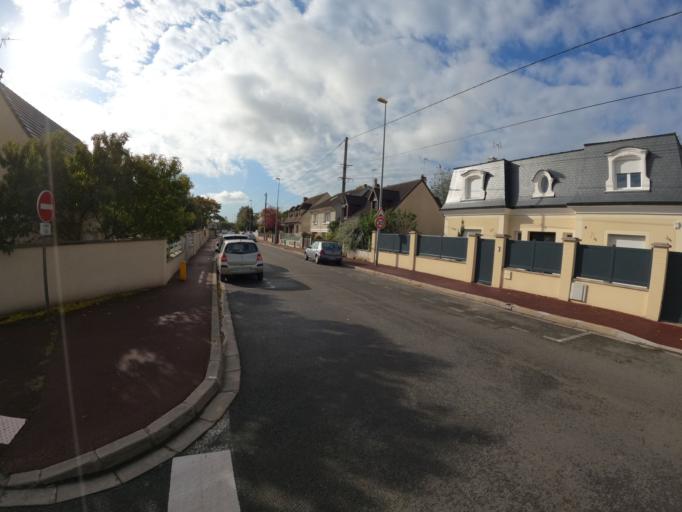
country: FR
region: Ile-de-France
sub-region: Departement de Seine-et-Marne
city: Chelles
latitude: 48.8911
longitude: 2.6057
